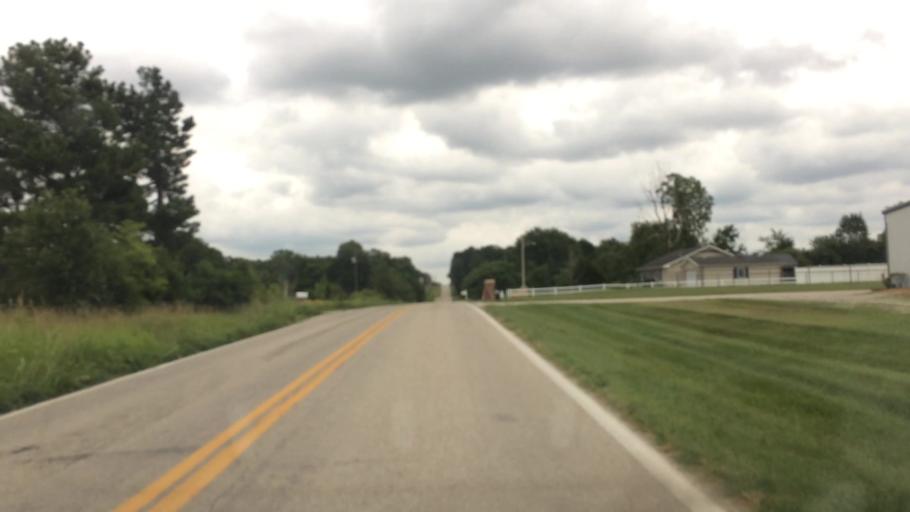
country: US
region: Missouri
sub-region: Greene County
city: Strafford
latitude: 37.3004
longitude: -93.1616
